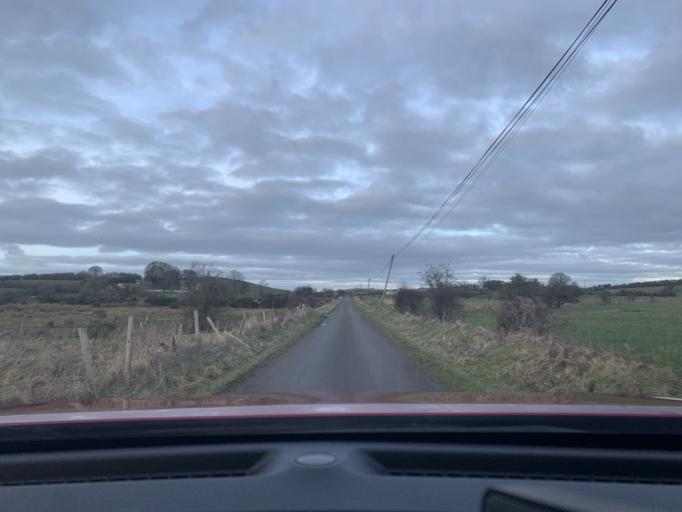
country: IE
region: Connaught
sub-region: Sligo
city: Ballymote
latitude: 54.0483
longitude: -8.5723
